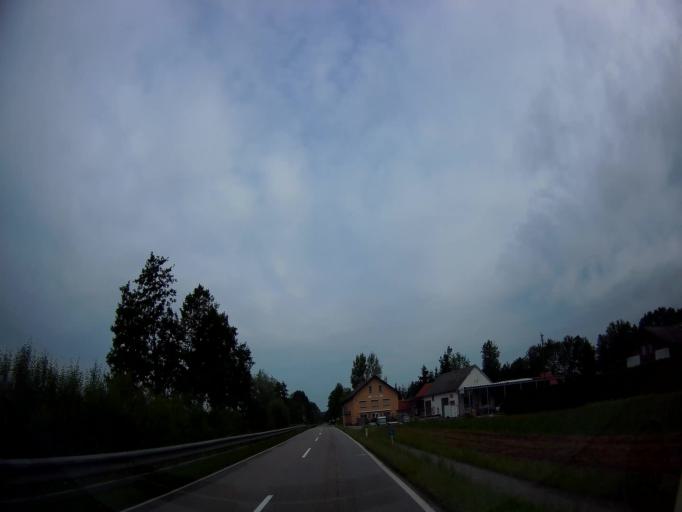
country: AT
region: Upper Austria
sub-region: Politischer Bezirk Braunau am Inn
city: Altheim
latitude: 48.1302
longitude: 13.1467
